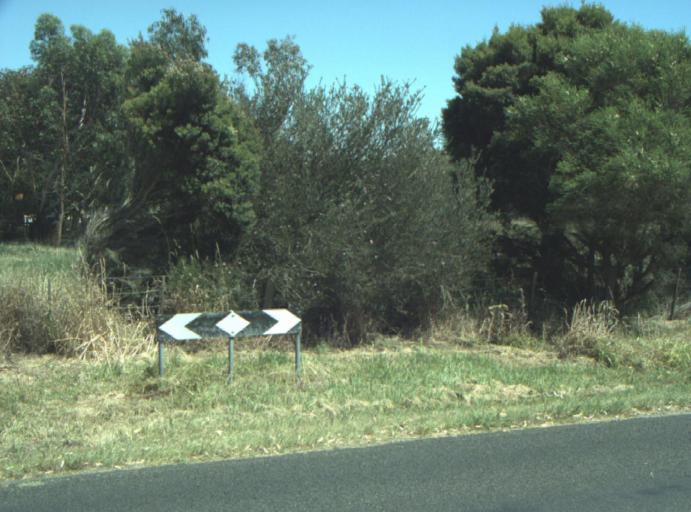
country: AU
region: Victoria
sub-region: Greater Geelong
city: Breakwater
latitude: -38.2527
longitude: 144.3504
